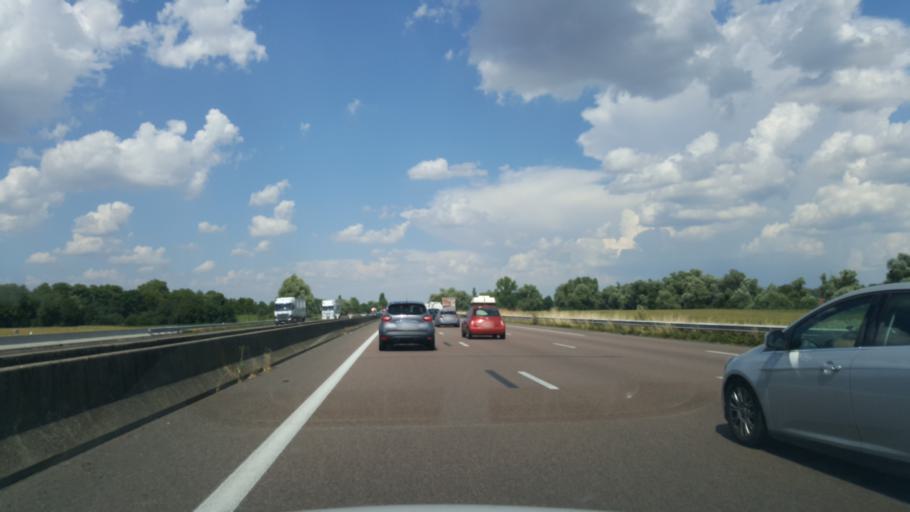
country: FR
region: Bourgogne
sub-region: Departement de Saone-et-Loire
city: Demigny
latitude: 46.9340
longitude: 4.8224
